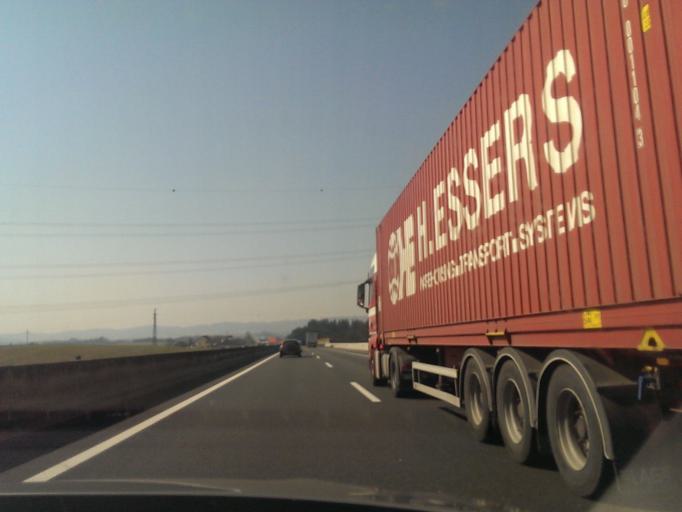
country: AT
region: Upper Austria
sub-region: Politischer Bezirk Vocklabruck
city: Niederthalheim
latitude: 48.1776
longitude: 13.7374
